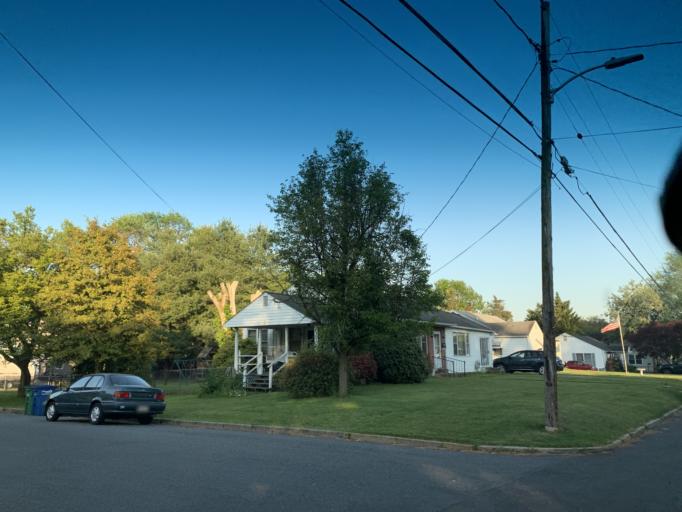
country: US
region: Maryland
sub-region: Harford County
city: Aberdeen
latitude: 39.5007
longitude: -76.1733
